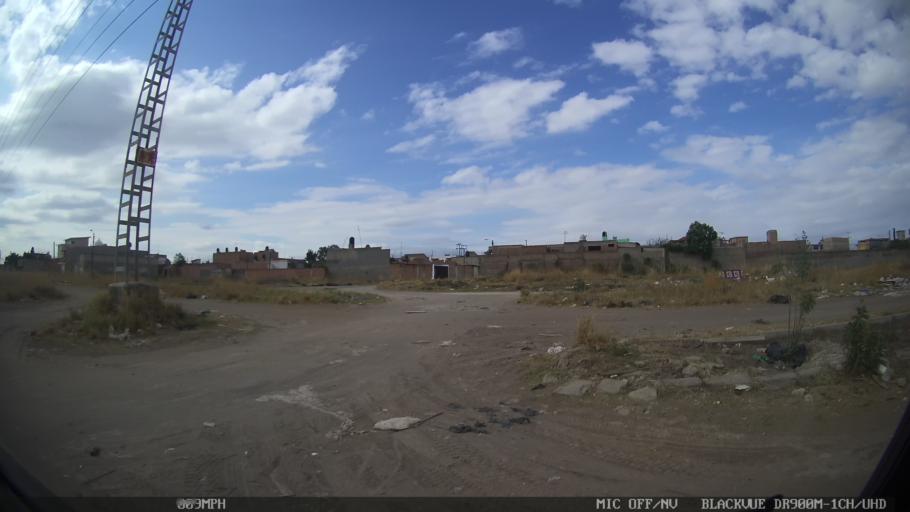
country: MX
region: Jalisco
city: Tonala
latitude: 20.6584
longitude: -103.2398
